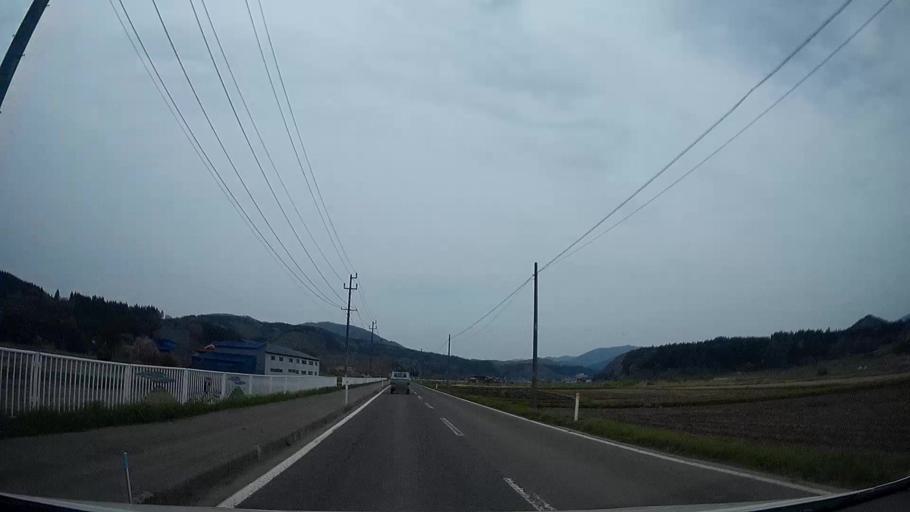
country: JP
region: Akita
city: Hanawa
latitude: 40.2822
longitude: 140.8018
